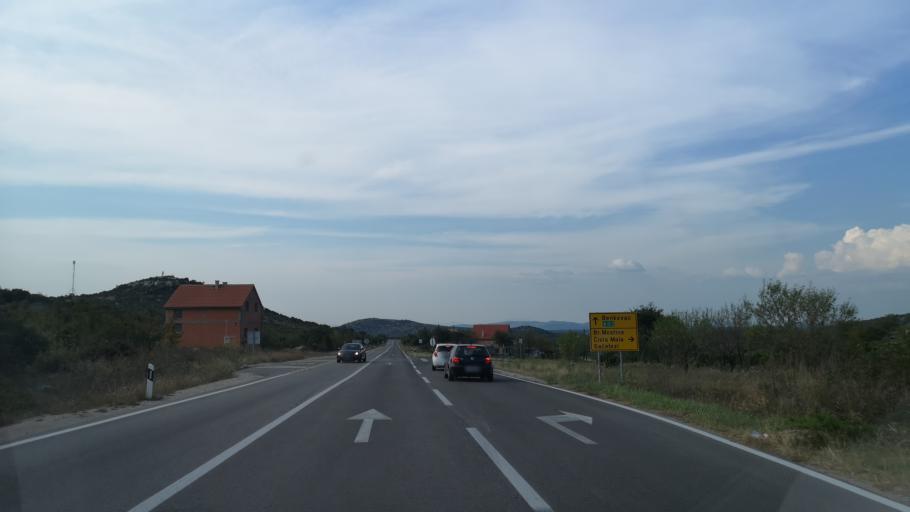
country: HR
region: Sibensko-Kniniska
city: Zaton
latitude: 43.8333
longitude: 15.7780
